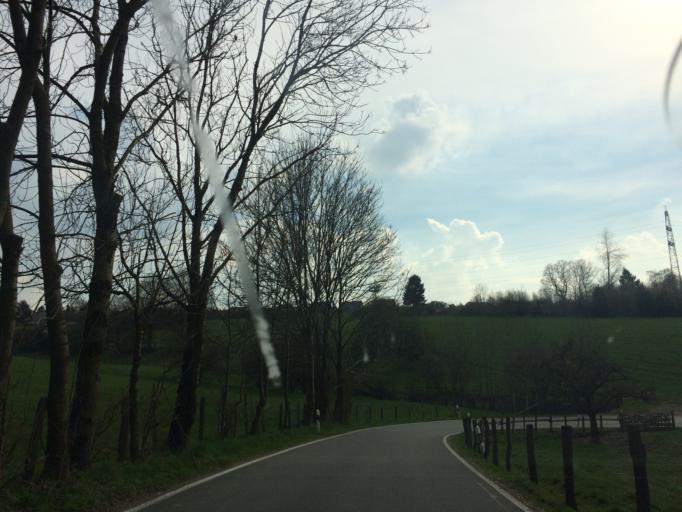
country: DE
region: North Rhine-Westphalia
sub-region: Regierungsbezirk Arnsberg
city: Nachrodt-Wiblingwerde
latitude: 51.3118
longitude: 7.6127
